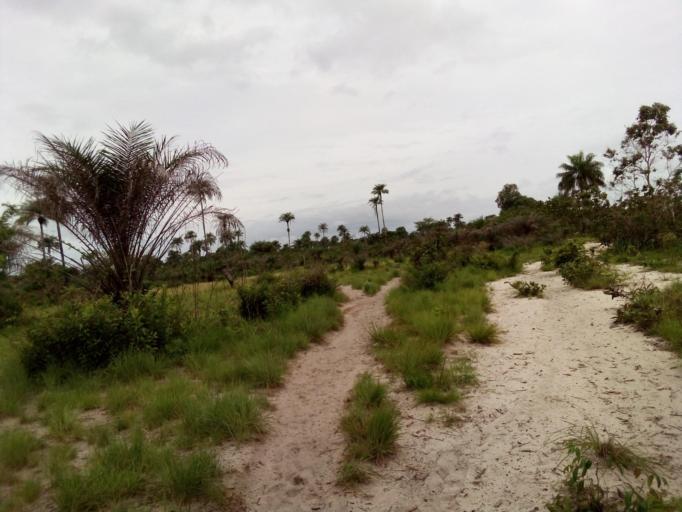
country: SL
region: Southern Province
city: Bonthe
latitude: 7.5205
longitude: -12.5744
